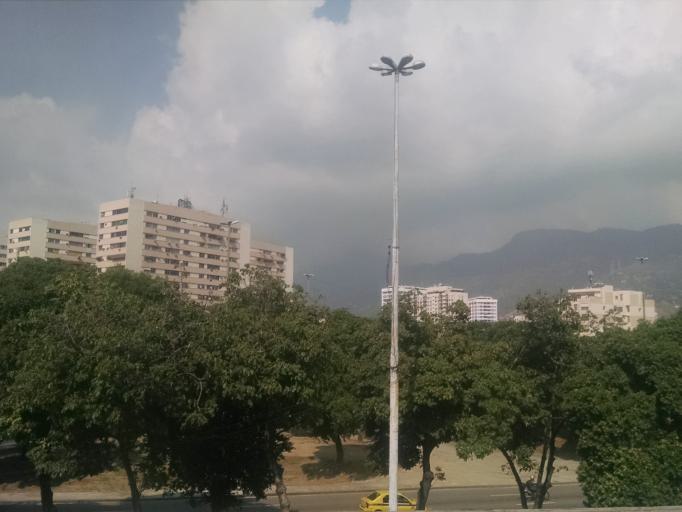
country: BR
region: Rio de Janeiro
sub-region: Rio De Janeiro
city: Rio de Janeiro
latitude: -22.9100
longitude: -43.2114
